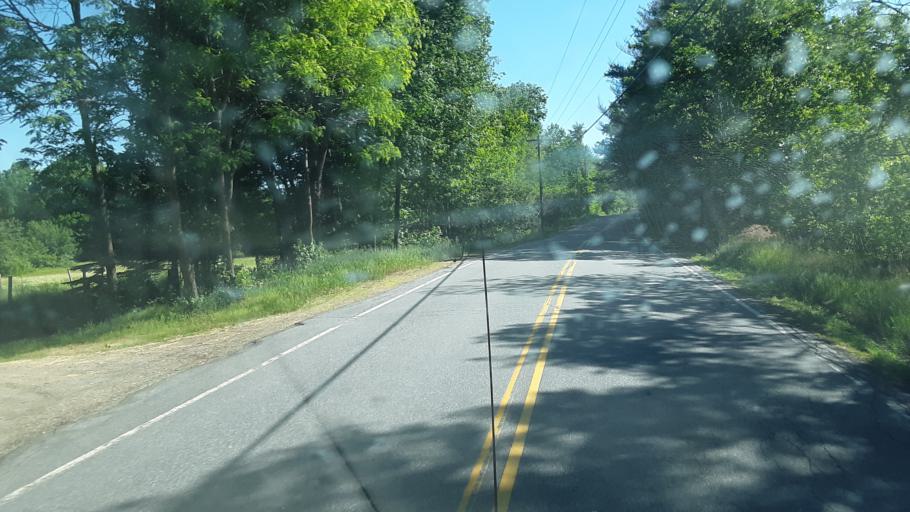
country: US
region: New Hampshire
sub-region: Grafton County
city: North Haverhill
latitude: 44.0943
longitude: -71.9440
